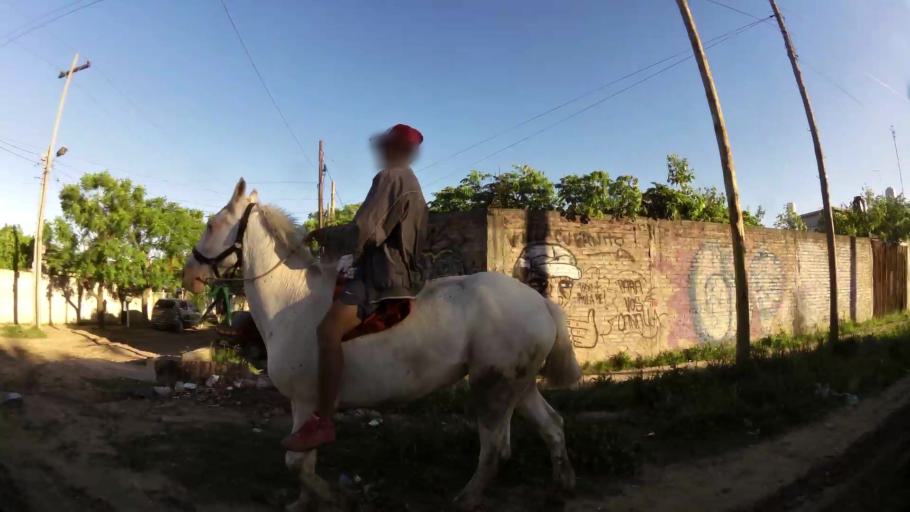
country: AR
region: Buenos Aires
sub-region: Partido de Almirante Brown
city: Adrogue
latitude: -34.7705
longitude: -58.3346
